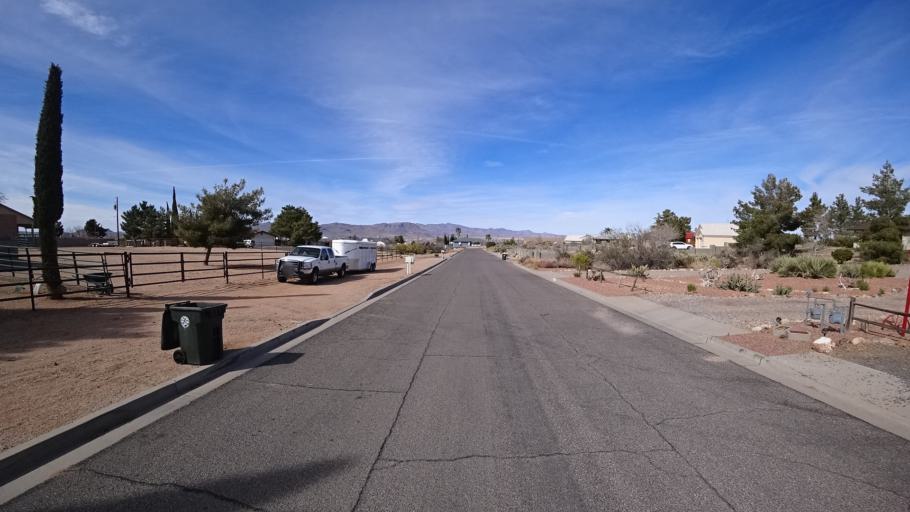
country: US
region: Arizona
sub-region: Mohave County
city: Kingman
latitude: 35.1847
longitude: -113.9897
